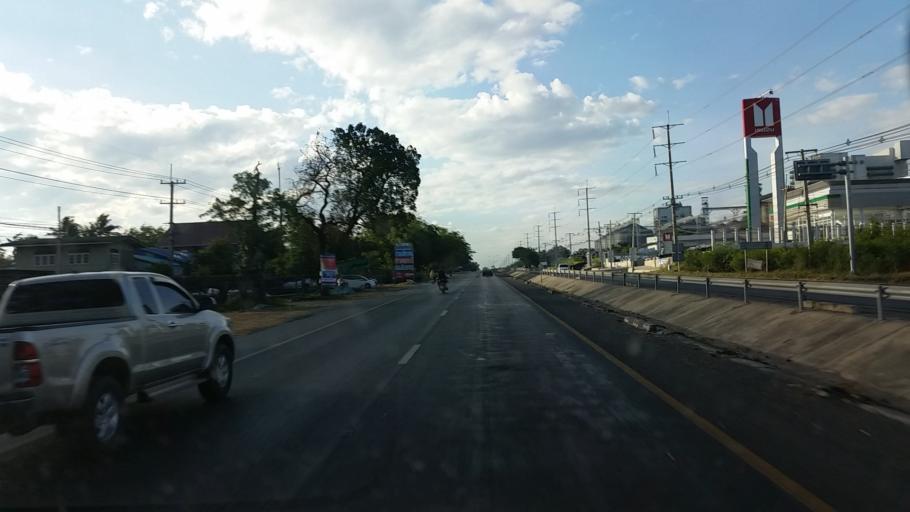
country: TH
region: Lop Buri
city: Phatthana Nikhom
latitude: 14.8193
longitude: 100.9112
